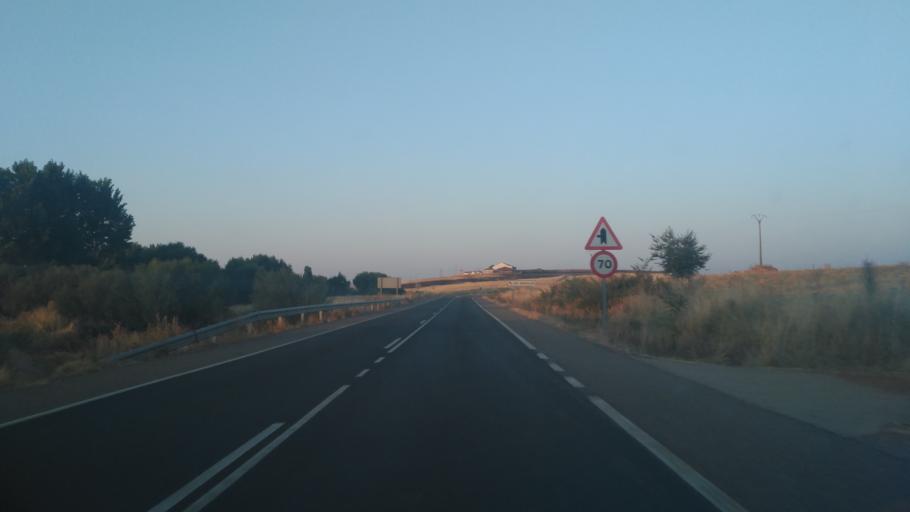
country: ES
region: Castille and Leon
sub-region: Provincia de Salamanca
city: Aldeatejada
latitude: 40.9131
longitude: -5.6996
